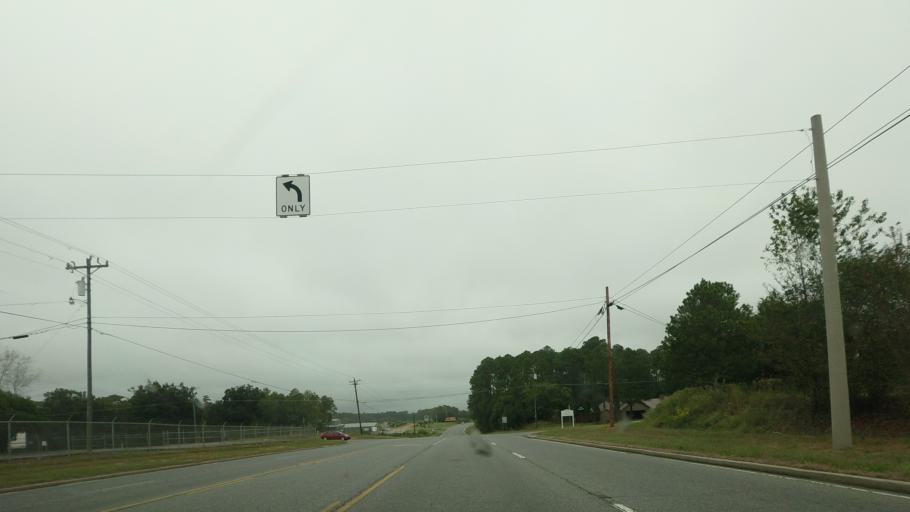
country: US
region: Georgia
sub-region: Irwin County
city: Ocilla
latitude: 31.6280
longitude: -83.2494
